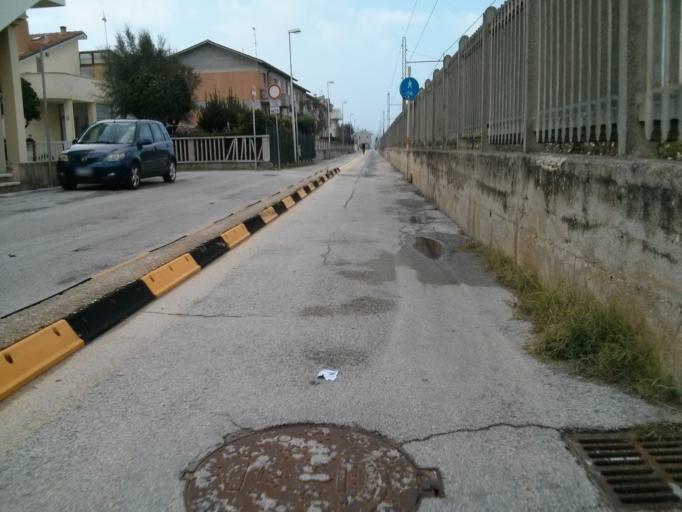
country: IT
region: The Marches
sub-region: Provincia di Pesaro e Urbino
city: Fano
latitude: 43.8582
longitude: 12.9979
